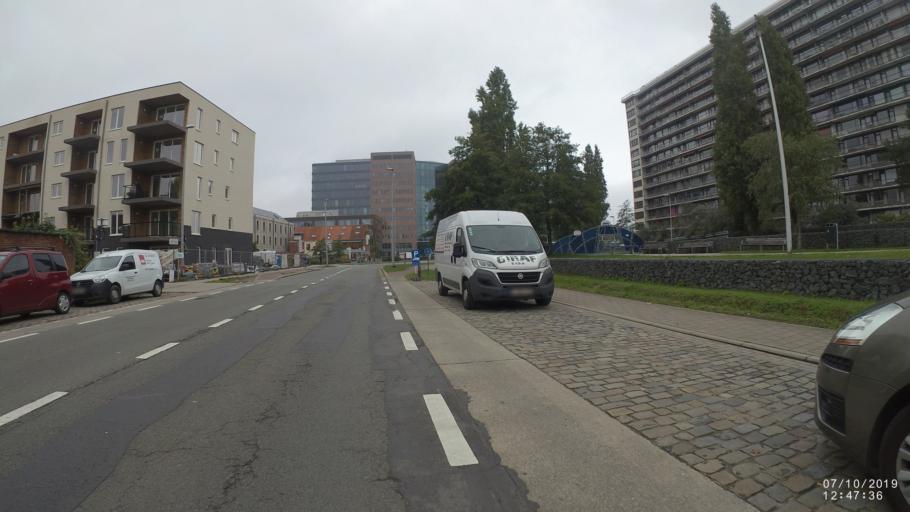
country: BE
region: Flanders
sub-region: Provincie Oost-Vlaanderen
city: Ledeberg
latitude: 51.0351
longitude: 3.7361
